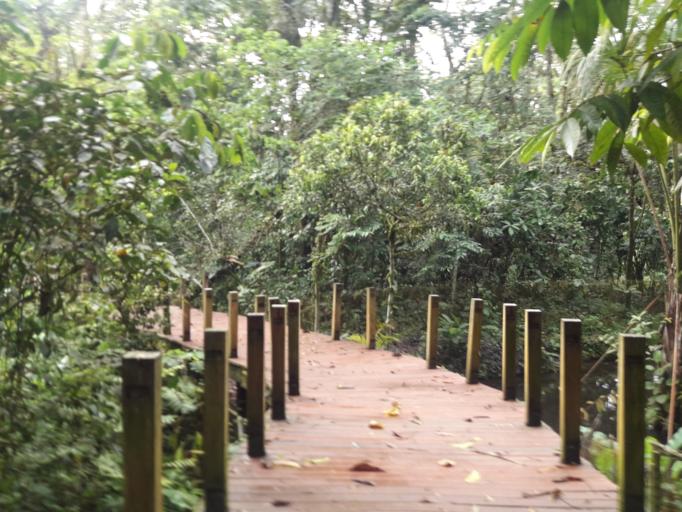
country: EC
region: Napo
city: Tena
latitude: -0.9951
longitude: -77.8163
